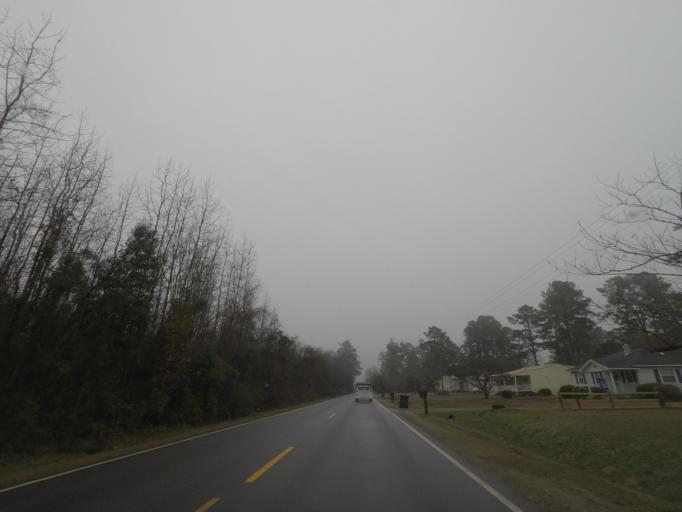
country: US
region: North Carolina
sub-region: Scotland County
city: Laurinburg
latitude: 34.8022
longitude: -79.4364
